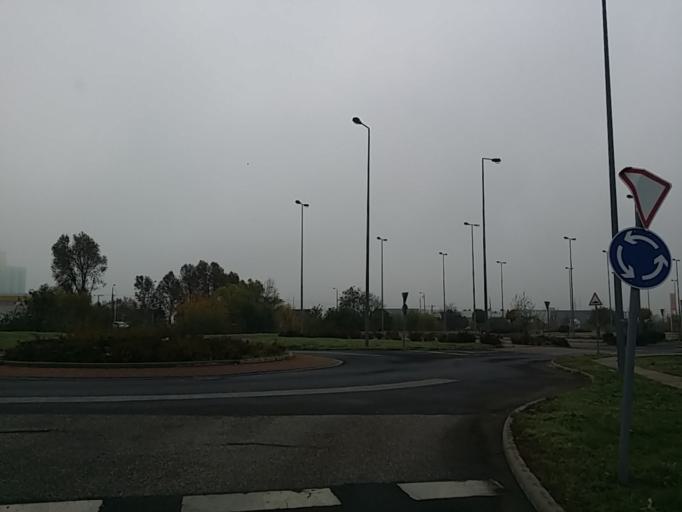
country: HU
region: Heves
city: Gyongyos
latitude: 47.7678
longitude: 19.9116
